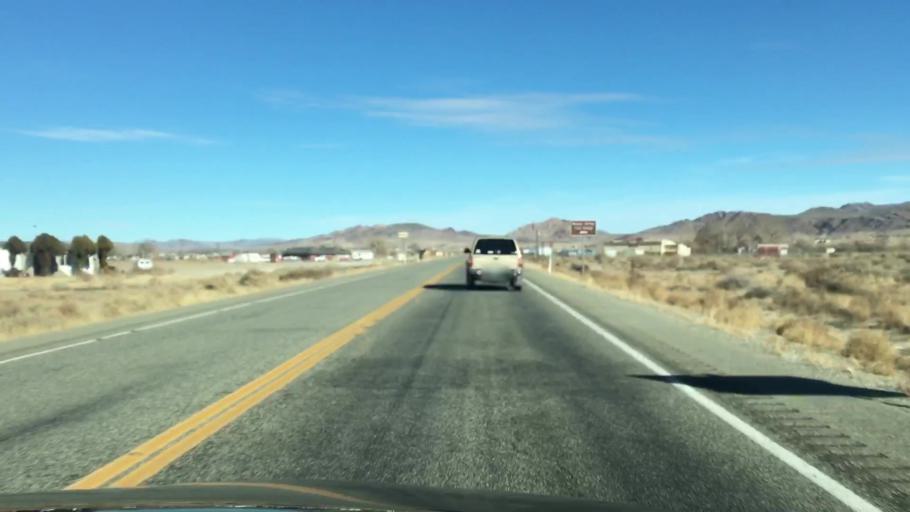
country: US
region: Nevada
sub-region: Lyon County
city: Yerington
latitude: 39.0083
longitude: -119.0817
